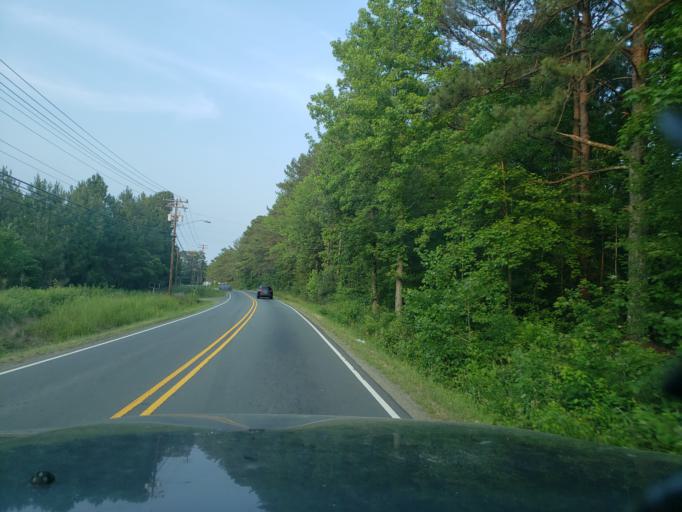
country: US
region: North Carolina
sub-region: Durham County
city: Durham
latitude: 35.9569
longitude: -78.8806
